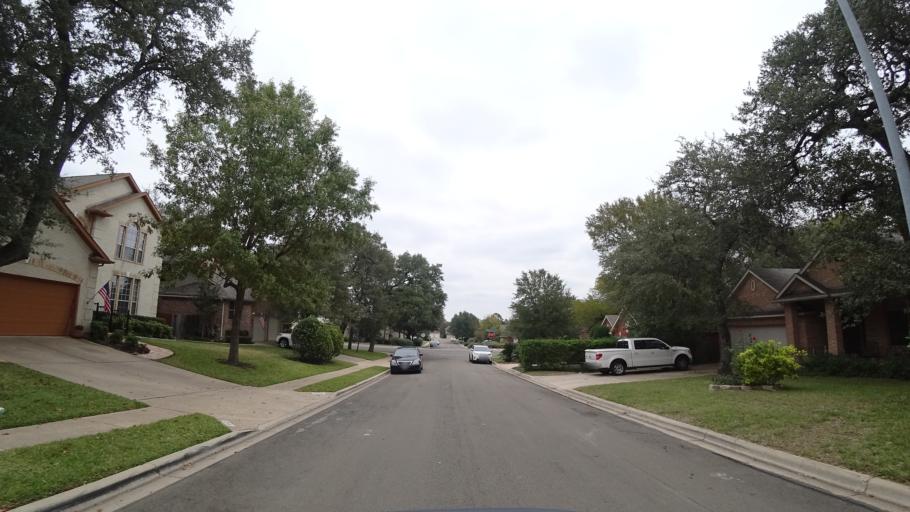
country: US
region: Texas
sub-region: Travis County
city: Shady Hollow
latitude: 30.2073
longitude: -97.8785
